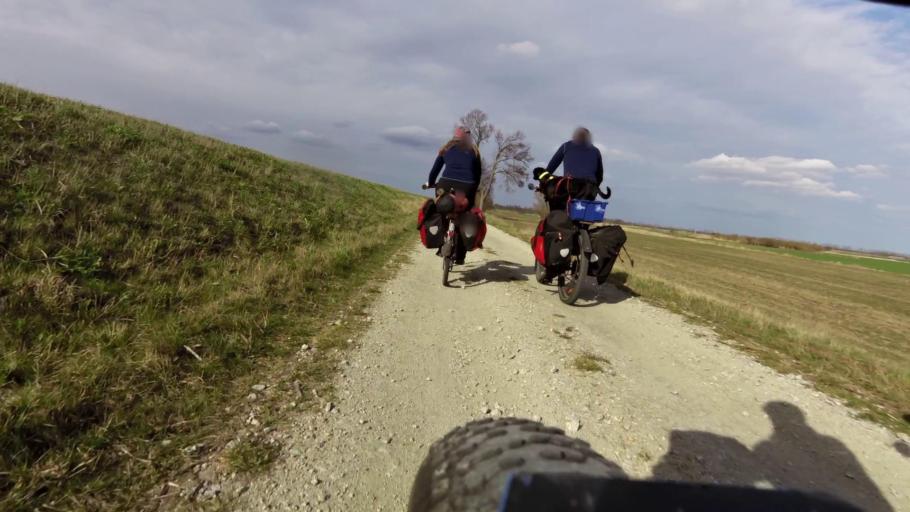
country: PL
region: Lubusz
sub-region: Powiat gorzowski
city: Kostrzyn nad Odra
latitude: 52.5470
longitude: 14.6199
